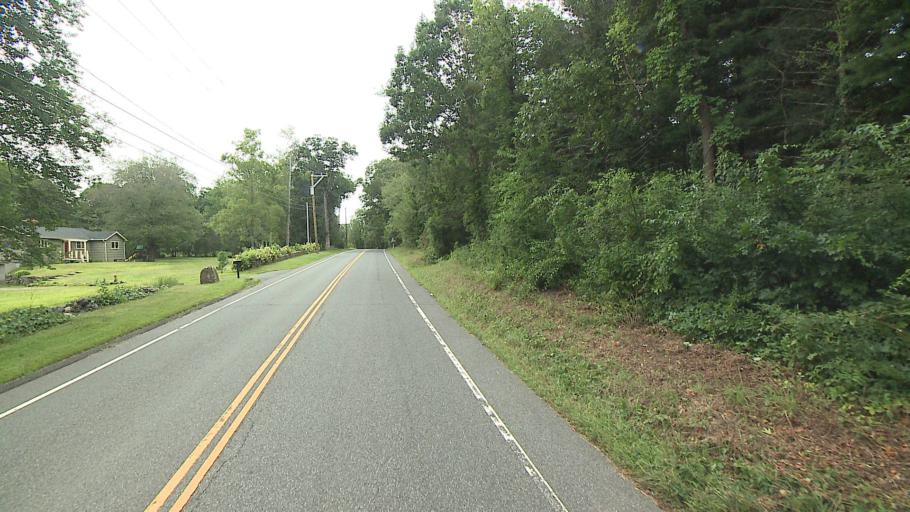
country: US
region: Connecticut
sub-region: Litchfield County
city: New Preston
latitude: 41.6151
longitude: -73.2916
